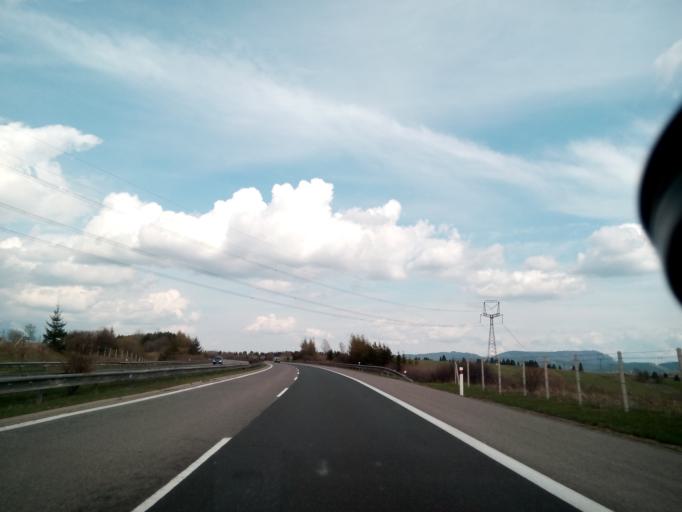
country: SK
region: Zilinsky
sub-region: Okres Liptovsky Mikulas
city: Hybe
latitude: 49.0509
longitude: 19.7856
